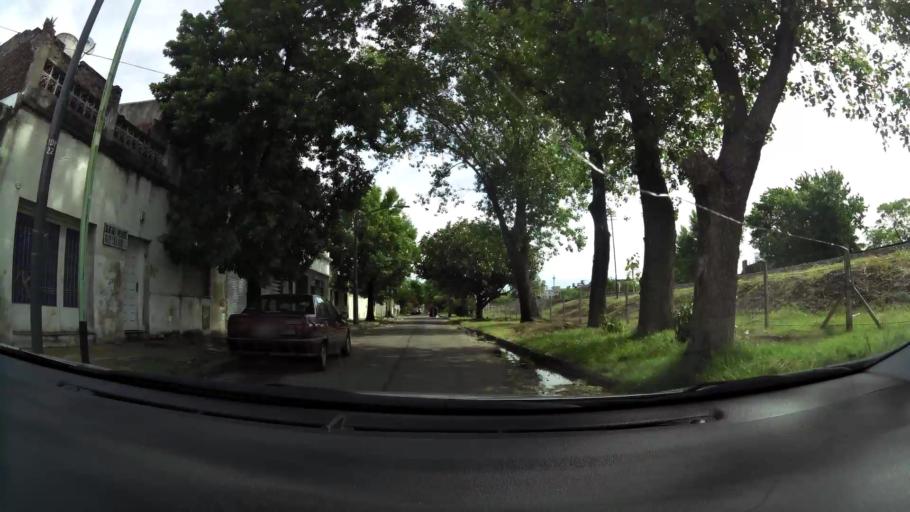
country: AR
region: Buenos Aires F.D.
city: Villa Lugano
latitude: -34.6565
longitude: -58.4315
